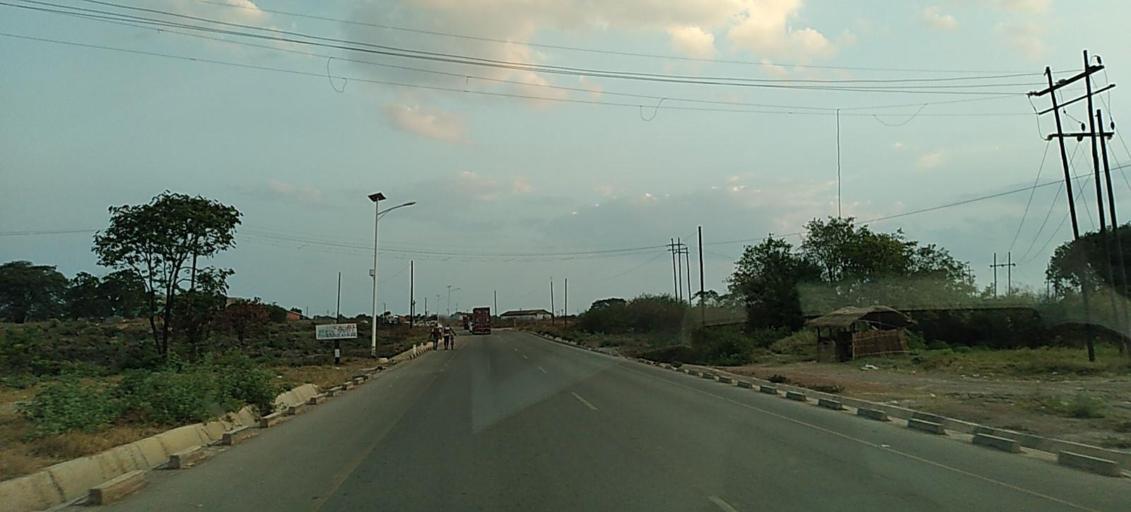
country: ZM
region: Copperbelt
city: Chingola
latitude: -12.5360
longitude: 27.8390
